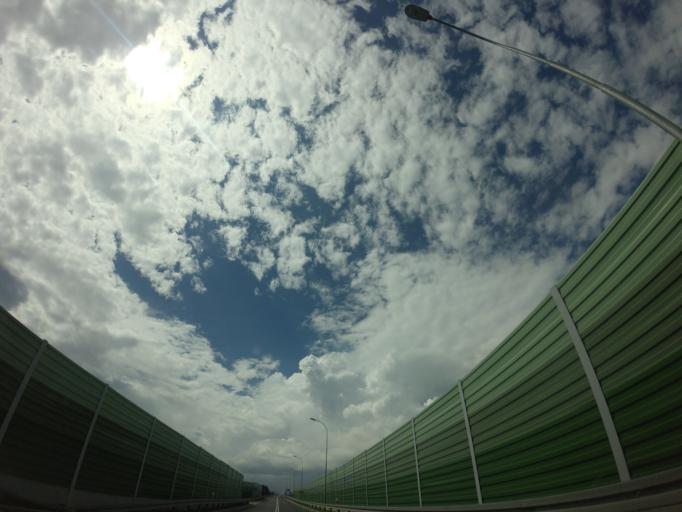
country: PL
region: Masovian Voivodeship
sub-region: Powiat lipski
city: Solec Nad Wisla
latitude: 51.1256
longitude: 21.8092
